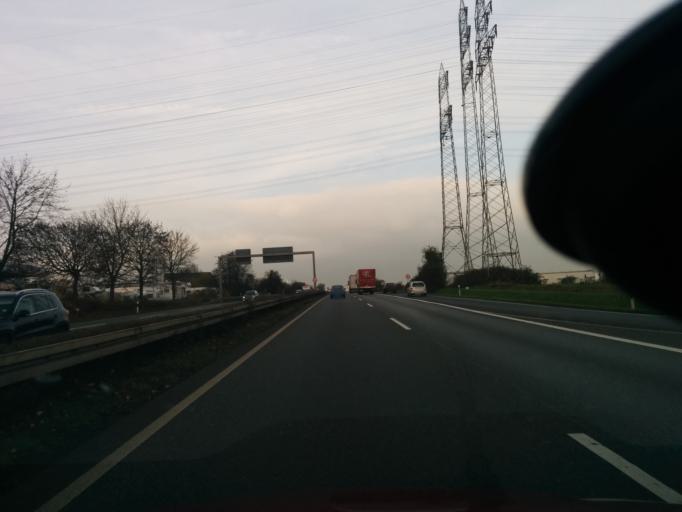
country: DE
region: Hesse
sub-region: Regierungsbezirk Giessen
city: Limburg an der Lahn
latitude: 50.4012
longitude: 8.0718
